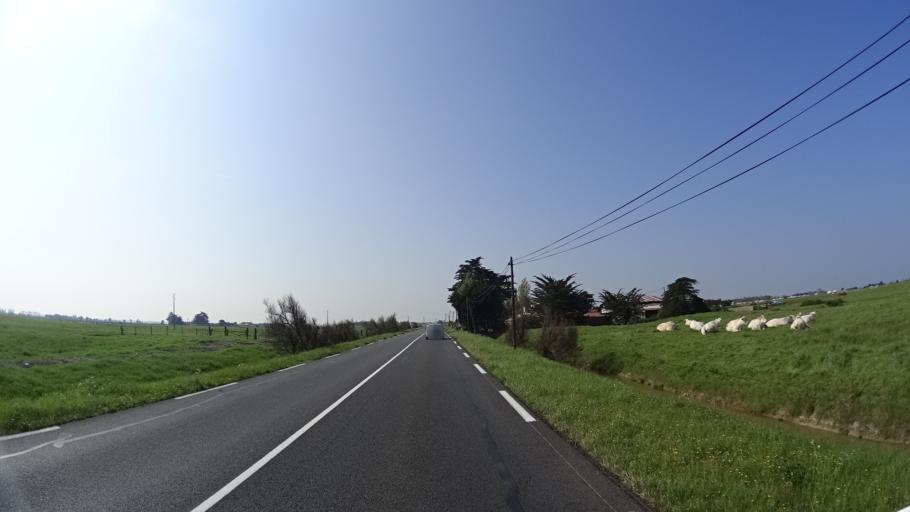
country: FR
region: Pays de la Loire
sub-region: Departement de la Vendee
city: Bouin
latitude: 46.9831
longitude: -1.9834
